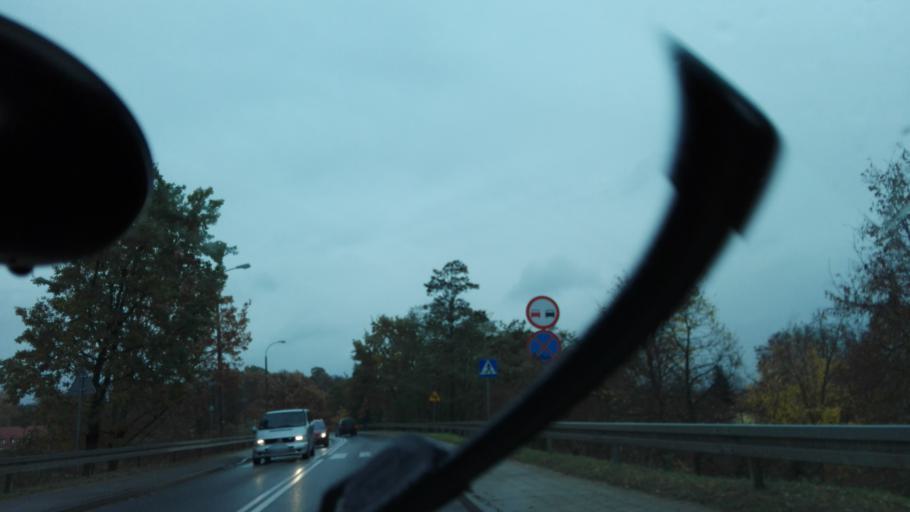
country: PL
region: Lublin Voivodeship
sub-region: Powiat pulawski
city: Pulawy
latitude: 51.4133
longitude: 21.9491
